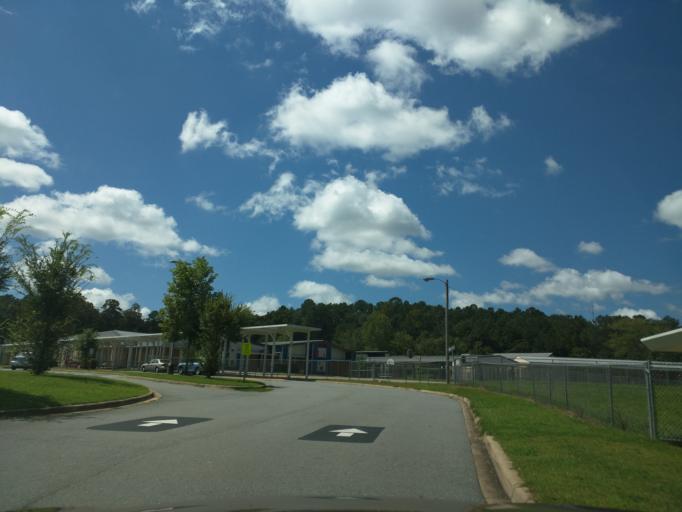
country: US
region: Florida
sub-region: Leon County
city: Tallahassee
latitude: 30.4367
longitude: -84.2153
